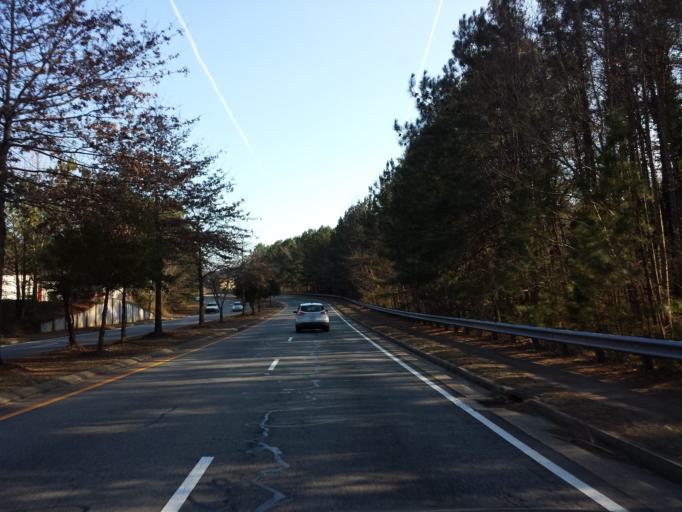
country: US
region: Georgia
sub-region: Cherokee County
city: Woodstock
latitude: 34.0340
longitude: -84.5310
